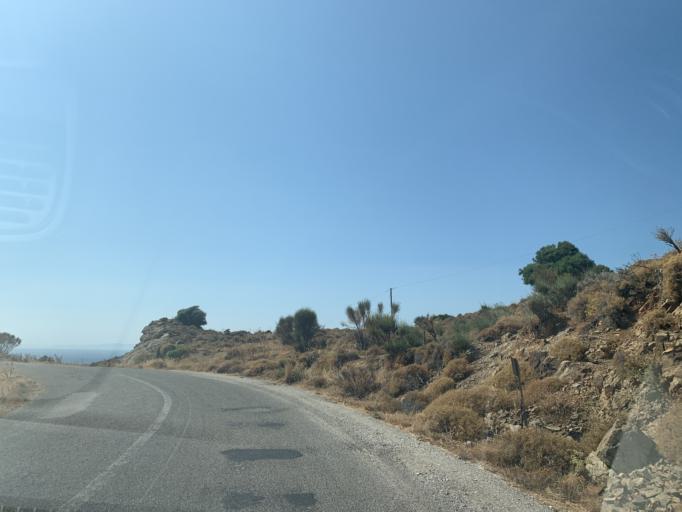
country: GR
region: North Aegean
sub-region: Chios
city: Vrontados
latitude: 38.4793
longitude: 25.8919
